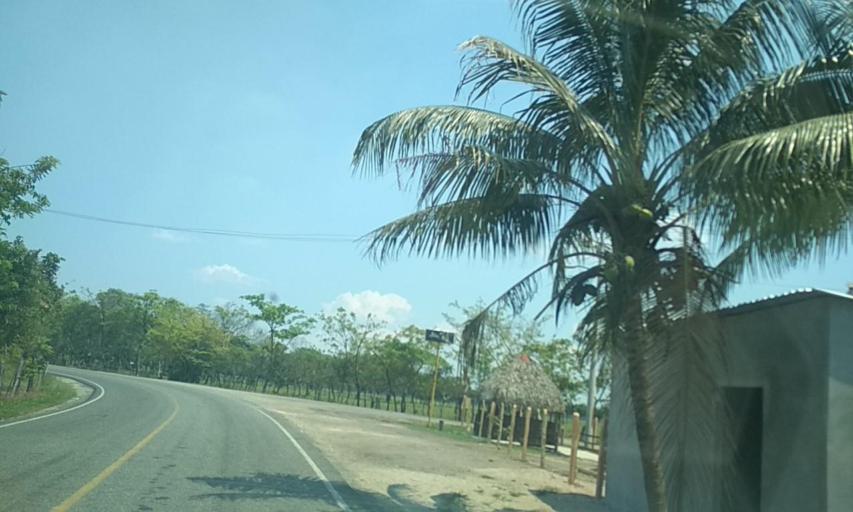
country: MX
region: Tabasco
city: Huimanguillo
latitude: 17.8022
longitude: -93.4904
